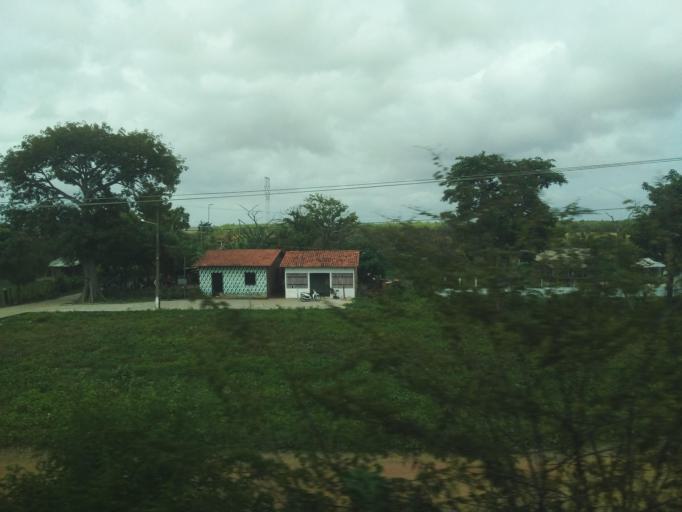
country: BR
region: Maranhao
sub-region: Icatu
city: Icatu
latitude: -2.9150
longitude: -44.3542
